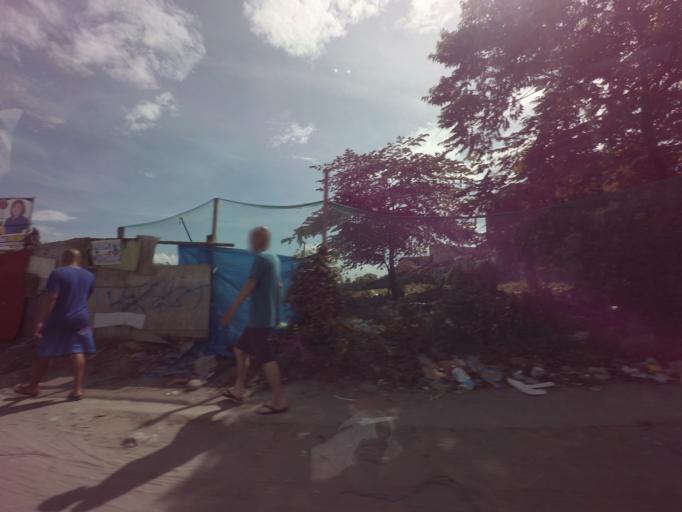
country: PH
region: Calabarzon
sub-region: Province of Rizal
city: Taguig
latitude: 14.5279
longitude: 121.0877
